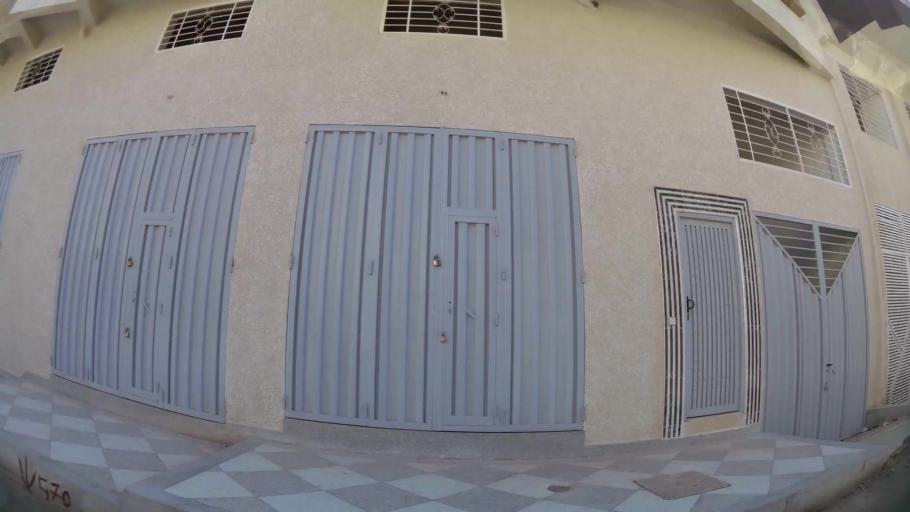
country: MA
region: Fes-Boulemane
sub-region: Fes
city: Fes
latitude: 33.9990
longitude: -5.0042
